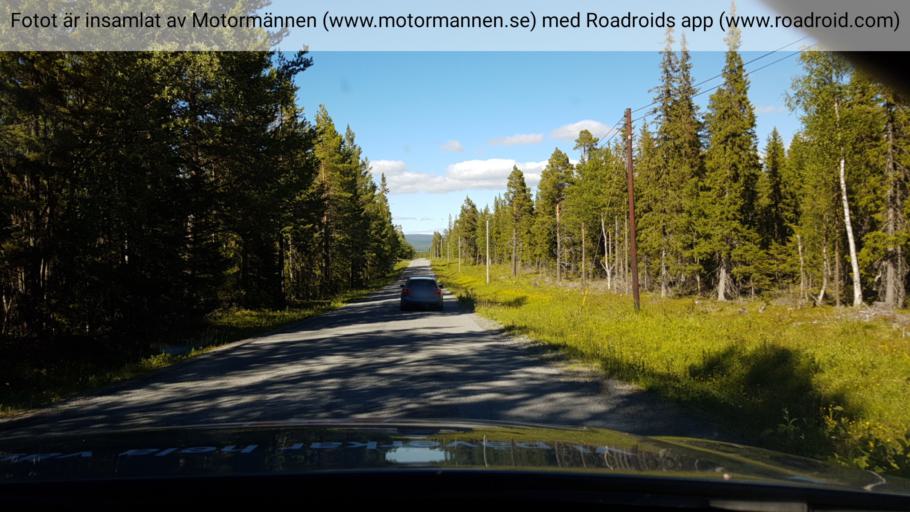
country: SE
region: Jaemtland
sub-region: Are Kommun
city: Are
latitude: 63.1633
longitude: 13.0734
